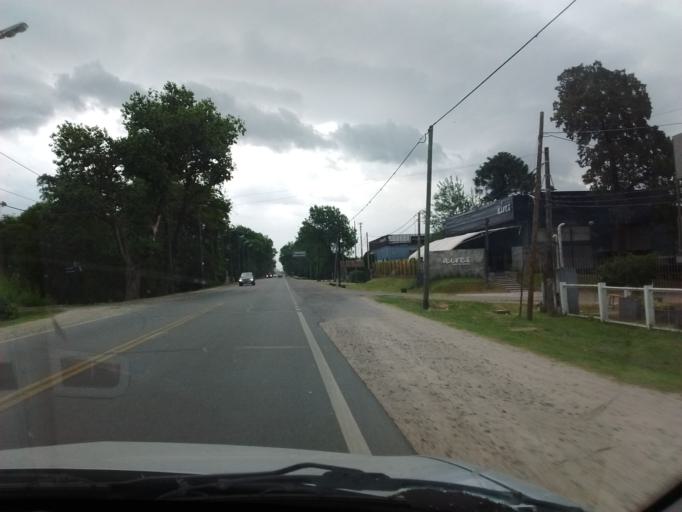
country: AR
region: Santa Fe
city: Funes
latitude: -32.9265
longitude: -60.7517
